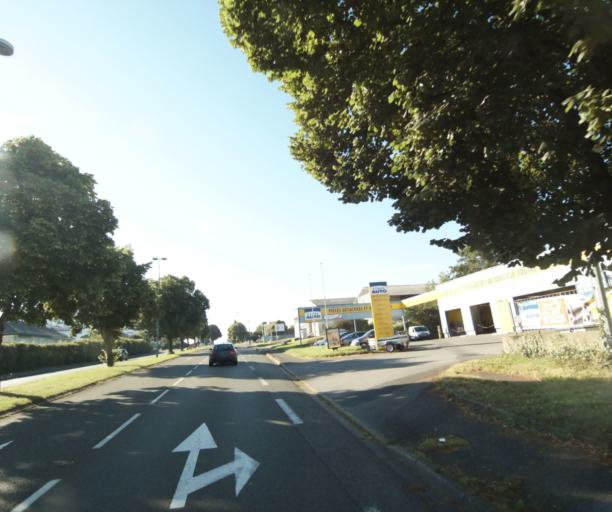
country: FR
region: Pays de la Loire
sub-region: Departement de la Mayenne
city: Laval
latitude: 48.0572
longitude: -0.7483
